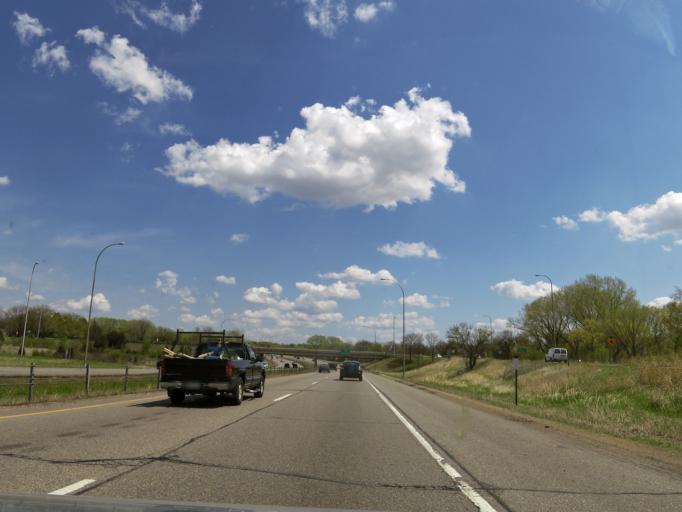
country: US
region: Minnesota
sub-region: Hennepin County
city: Edina
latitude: 44.8876
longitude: -93.3717
